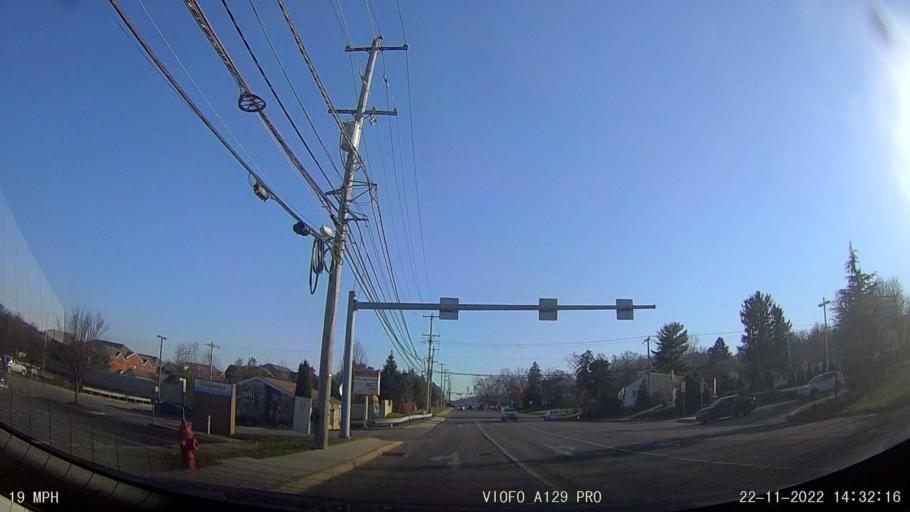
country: US
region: Pennsylvania
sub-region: Montgomery County
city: Bridgeport
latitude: 40.0940
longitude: -75.3622
